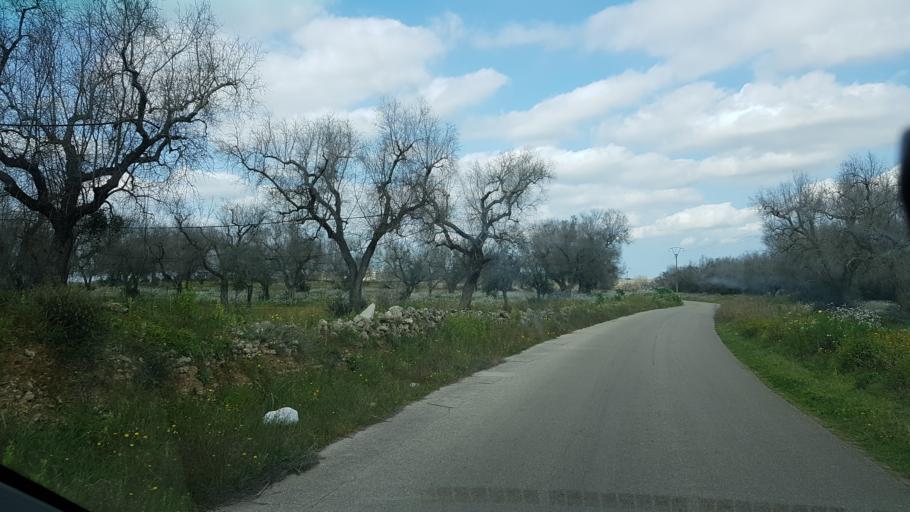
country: IT
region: Apulia
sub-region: Provincia di Brindisi
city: Torchiarolo
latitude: 40.4663
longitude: 18.0737
